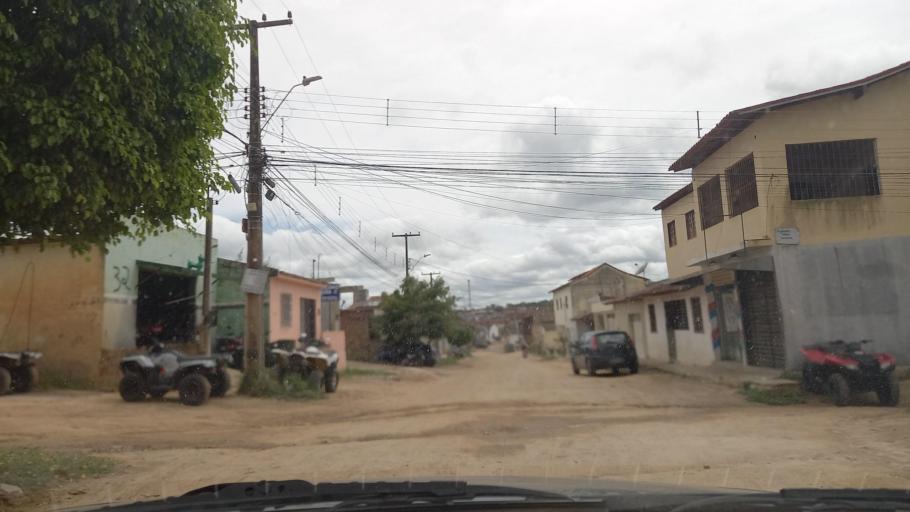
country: ET
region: Oromiya
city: Gore
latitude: 8.1961
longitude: 35.5798
